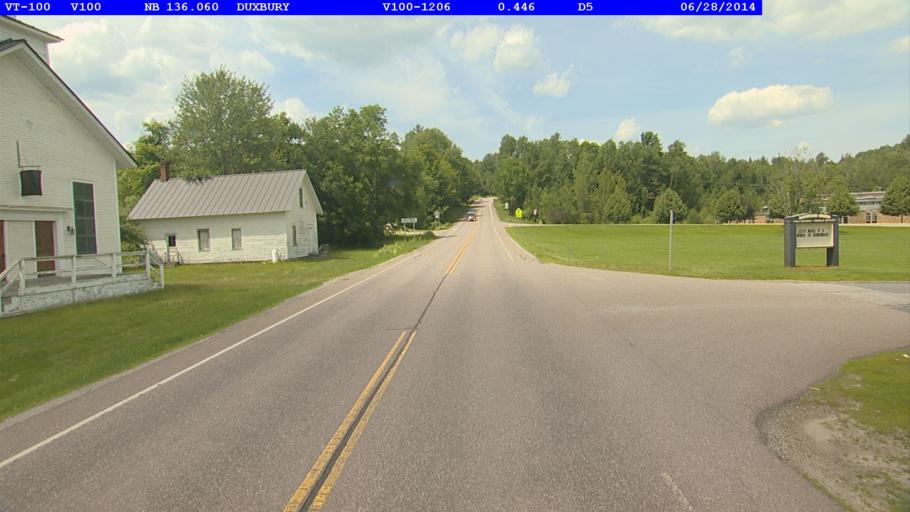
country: US
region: Vermont
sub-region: Washington County
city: Waterbury
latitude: 44.2529
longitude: -72.7881
